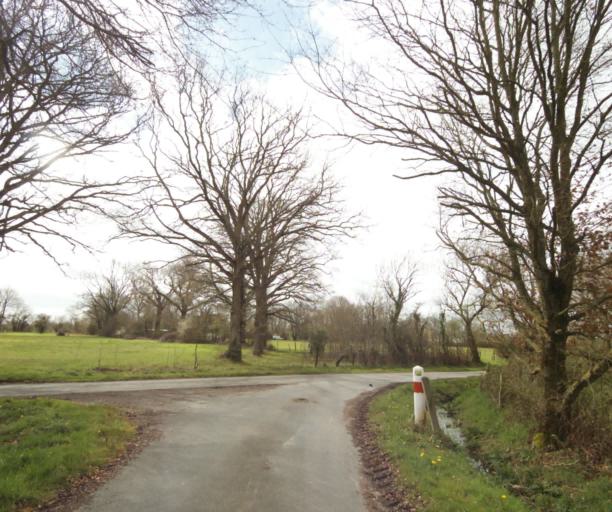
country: FR
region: Pays de la Loire
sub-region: Departement de la Loire-Atlantique
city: Bouvron
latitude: 47.4382
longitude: -1.8574
